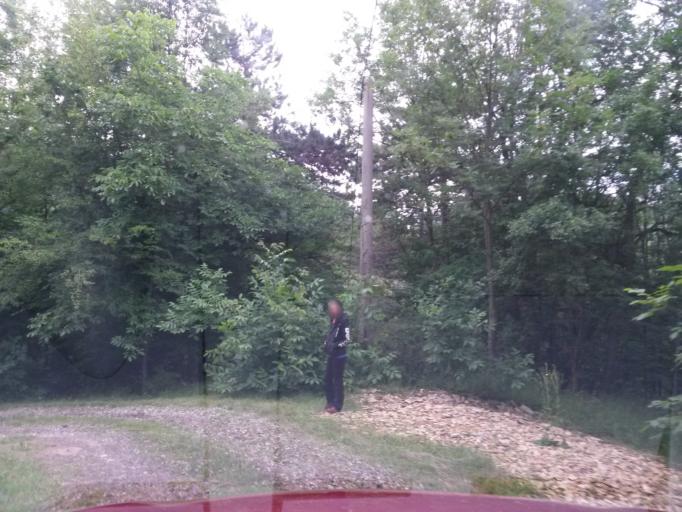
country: SK
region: Banskobystricky
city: Detva
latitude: 48.4175
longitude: 19.3582
